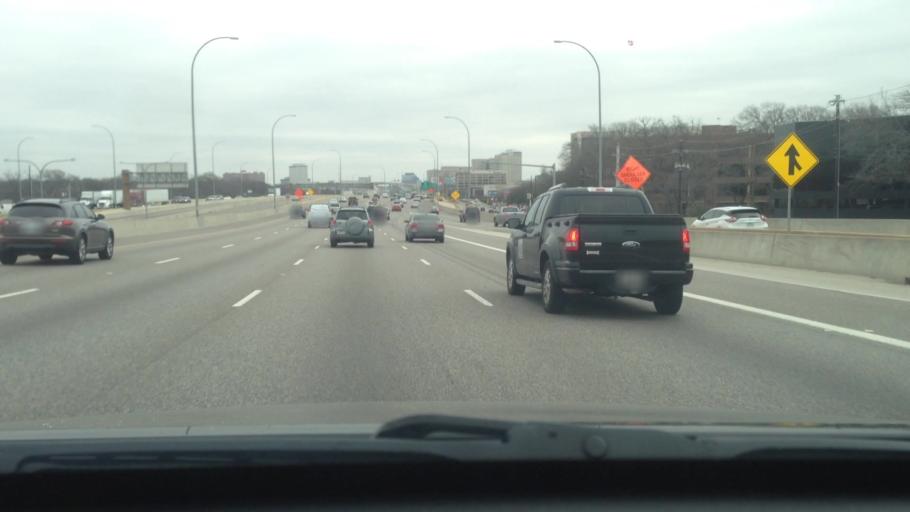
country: US
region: Texas
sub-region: Dallas County
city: Addison
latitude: 32.9247
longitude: -96.7901
